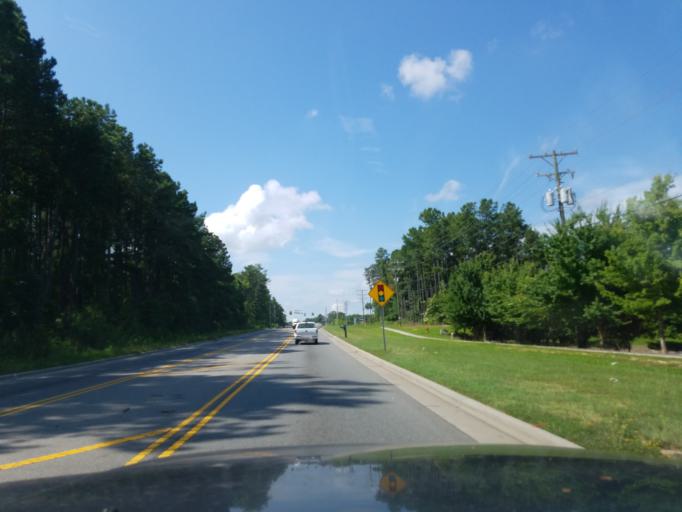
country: US
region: North Carolina
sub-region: Durham County
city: Durham
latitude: 35.9447
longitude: -78.9049
